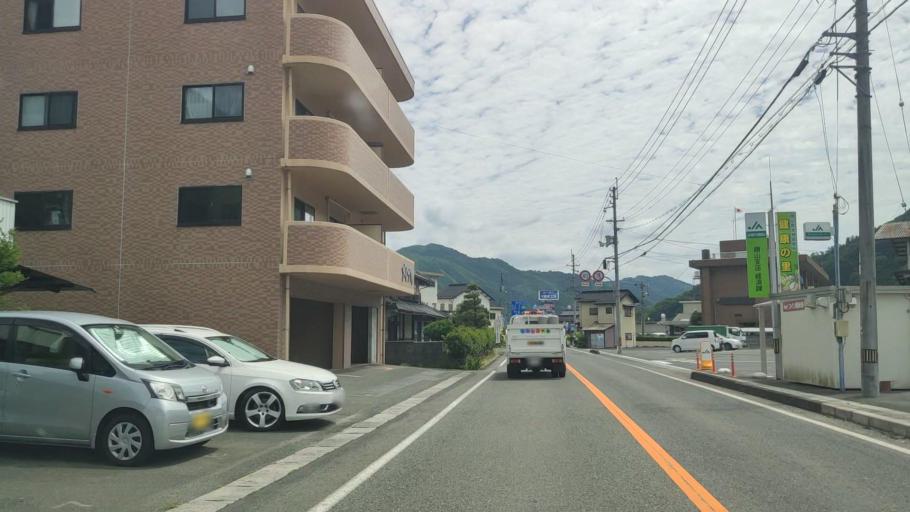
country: JP
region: Okayama
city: Niimi
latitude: 35.0766
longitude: 133.6872
